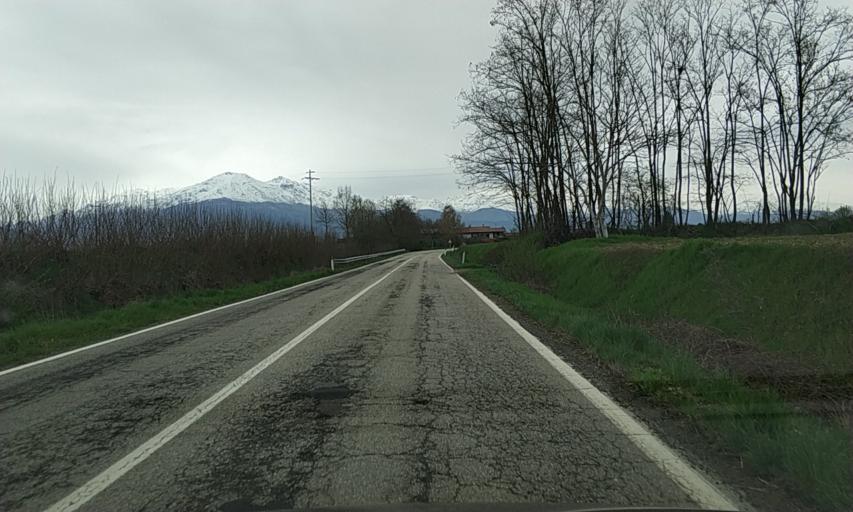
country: IT
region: Piedmont
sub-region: Provincia di Torino
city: Favria
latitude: 45.3121
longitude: 7.6782
